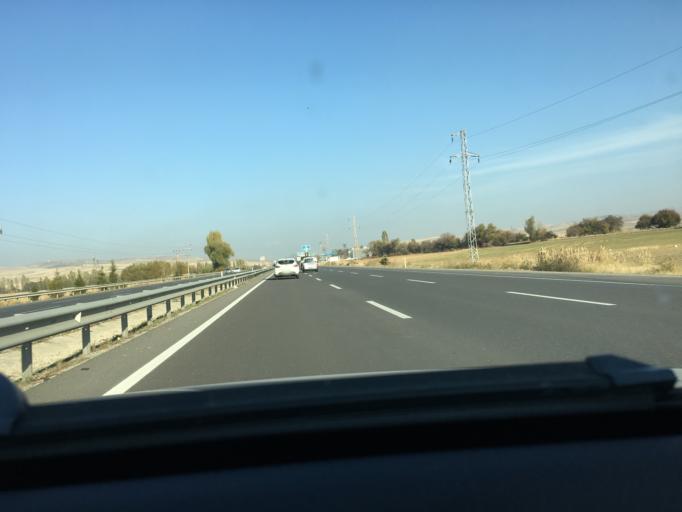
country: TR
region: Ankara
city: Temelli
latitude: 39.7519
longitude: 32.4365
